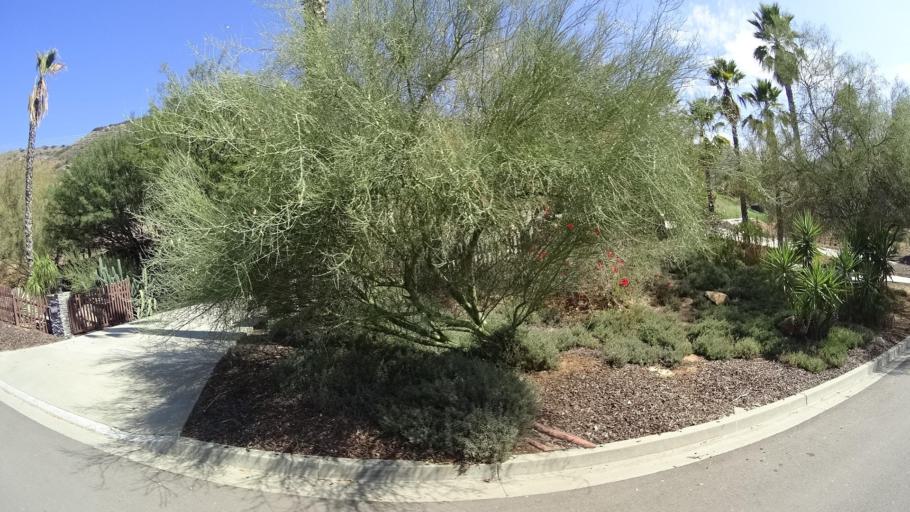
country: US
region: California
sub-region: San Diego County
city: Crest
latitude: 32.7828
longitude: -116.8738
